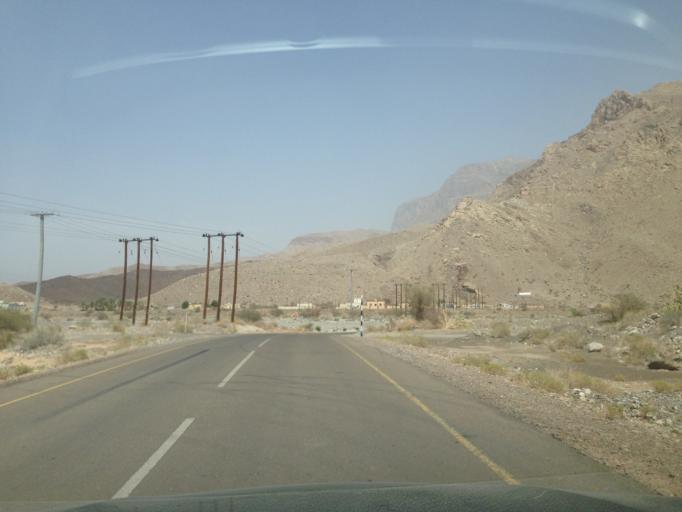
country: OM
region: Az Zahirah
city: `Ibri
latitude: 23.1763
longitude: 56.9133
